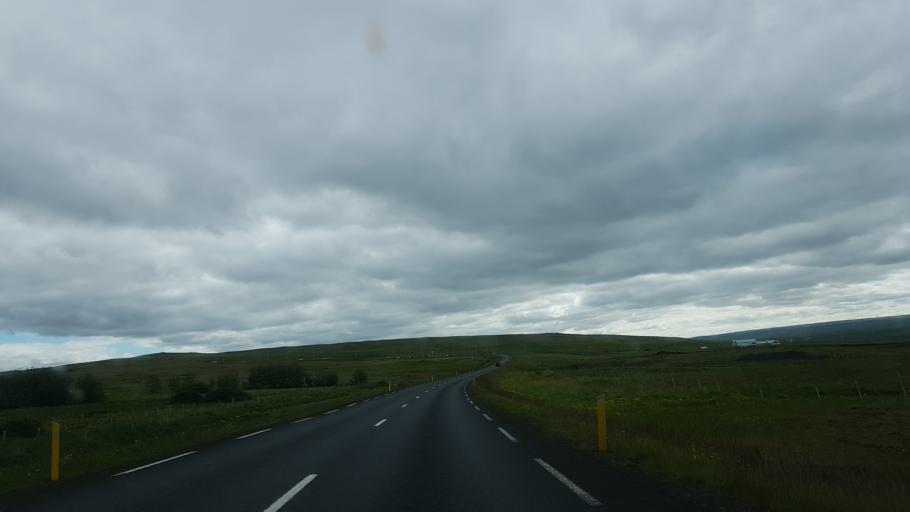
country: IS
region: Northwest
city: Saudarkrokur
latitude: 65.3592
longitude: -20.8903
